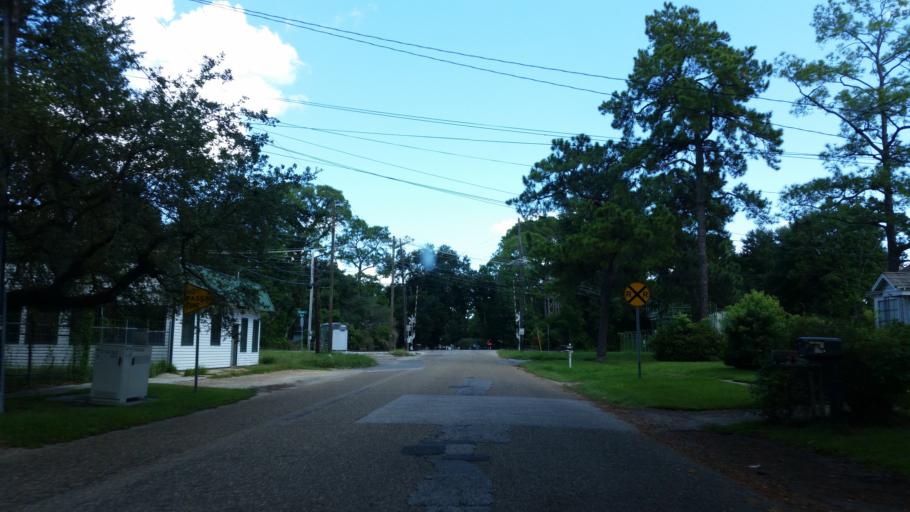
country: US
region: Alabama
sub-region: Mobile County
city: Mobile
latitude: 30.6785
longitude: -88.0924
